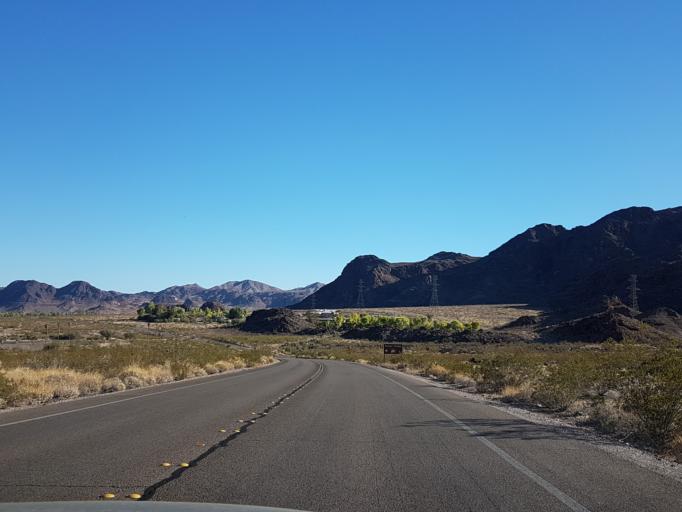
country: US
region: Nevada
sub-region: Clark County
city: Boulder City
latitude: 36.0507
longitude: -114.8190
